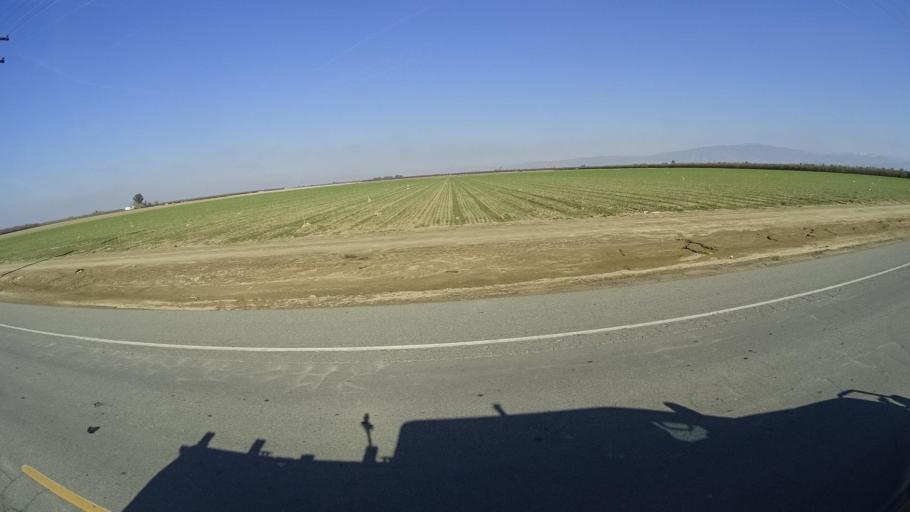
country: US
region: California
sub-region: Kern County
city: Arvin
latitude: 35.1945
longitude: -118.8537
